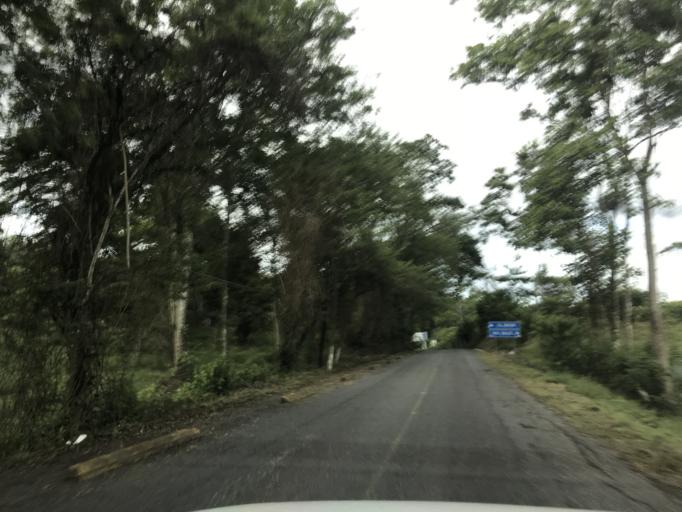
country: GT
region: Izabal
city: Morales
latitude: 15.6468
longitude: -89.0091
